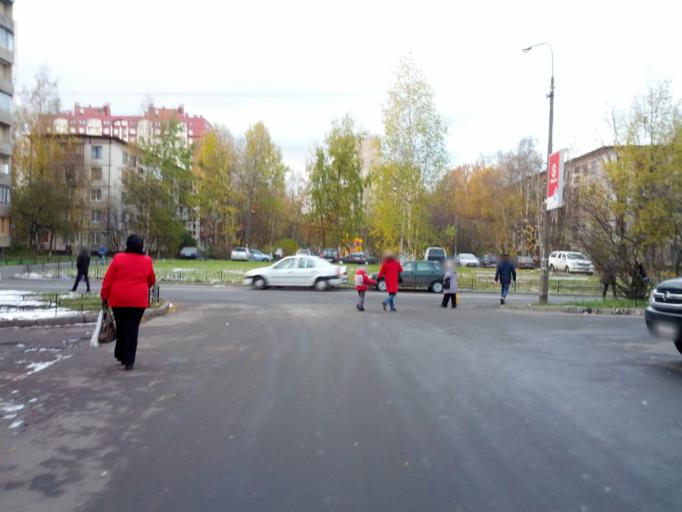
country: RU
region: St.-Petersburg
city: Obukhovo
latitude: 59.9004
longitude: 30.4790
